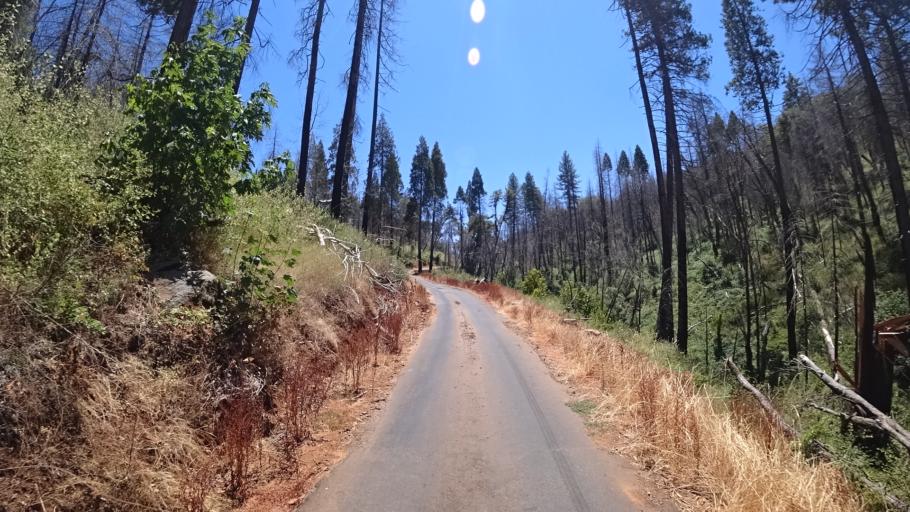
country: US
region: California
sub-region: Calaveras County
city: Mountain Ranch
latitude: 38.2519
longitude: -120.5795
